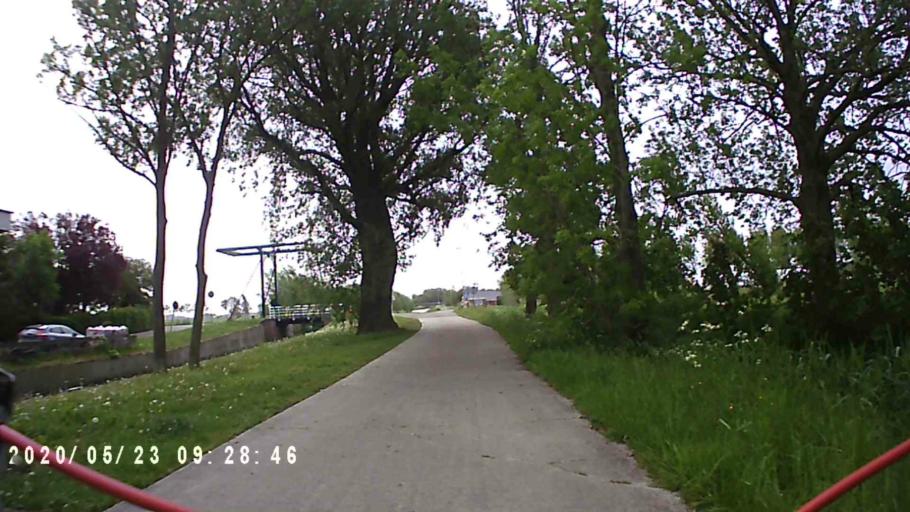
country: NL
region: Groningen
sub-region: Gemeente Bedum
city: Bedum
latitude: 53.2869
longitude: 6.7048
